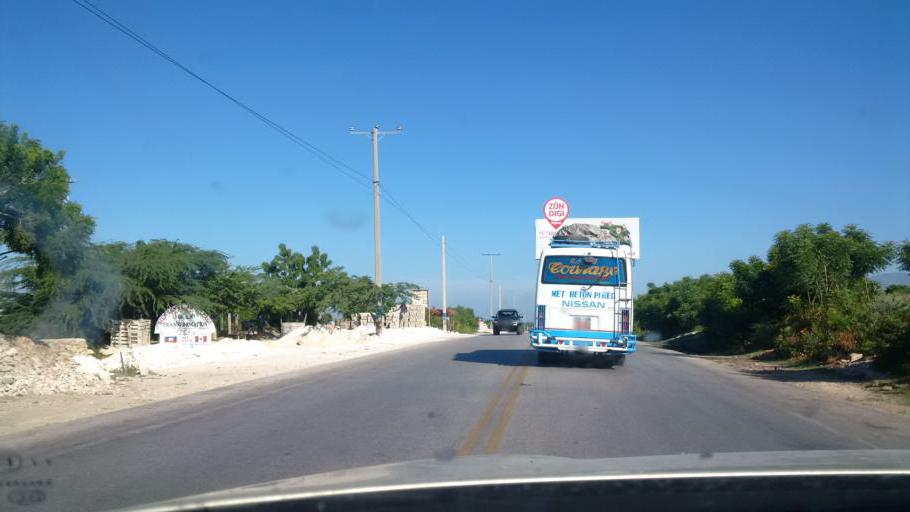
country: HT
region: Ouest
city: Cabaret
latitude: 18.7309
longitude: -72.3979
